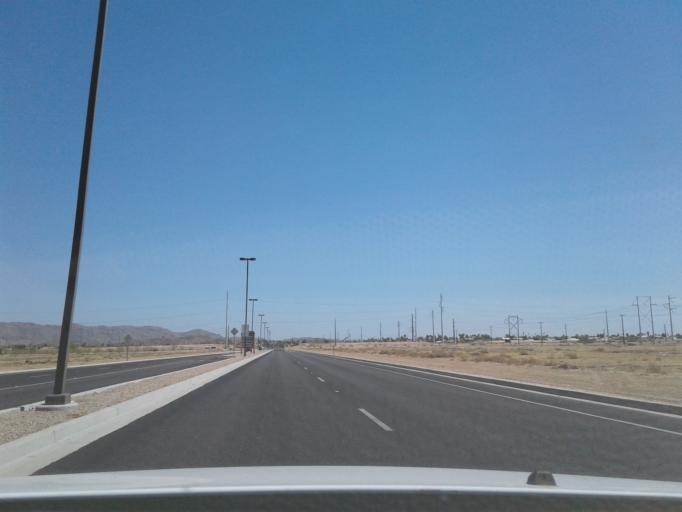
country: US
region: Arizona
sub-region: Maricopa County
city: Guadalupe
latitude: 33.2858
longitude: -111.9971
